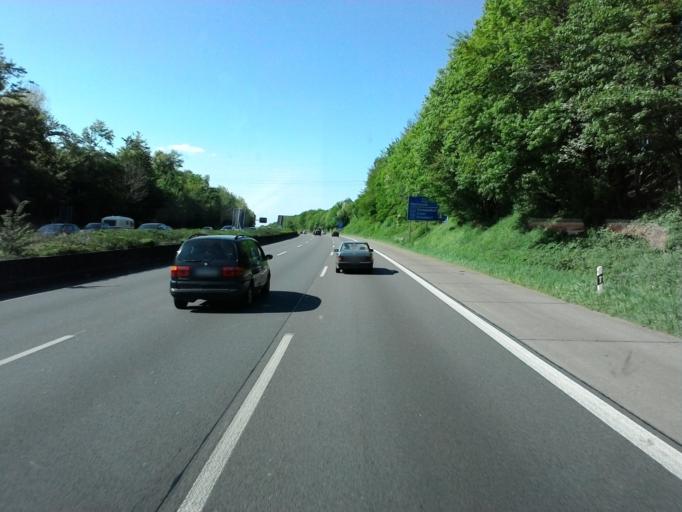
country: DE
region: North Rhine-Westphalia
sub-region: Regierungsbezirk Dusseldorf
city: Erkrath
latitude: 51.2672
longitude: 6.9140
